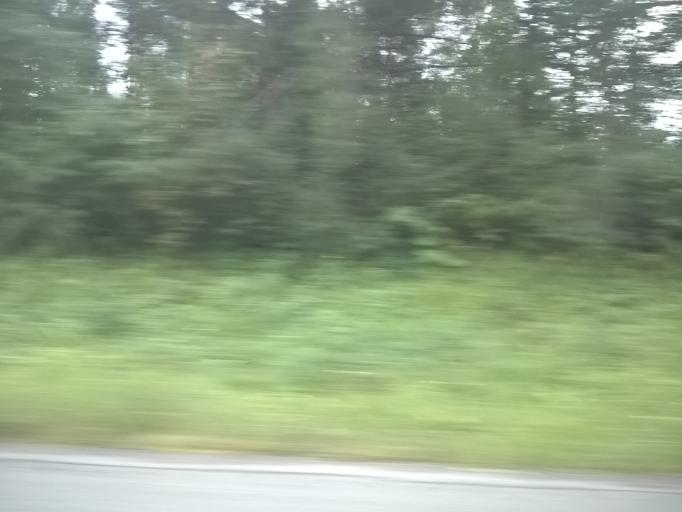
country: FI
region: Pirkanmaa
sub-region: Tampere
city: Tampere
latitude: 61.4977
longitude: 23.8142
